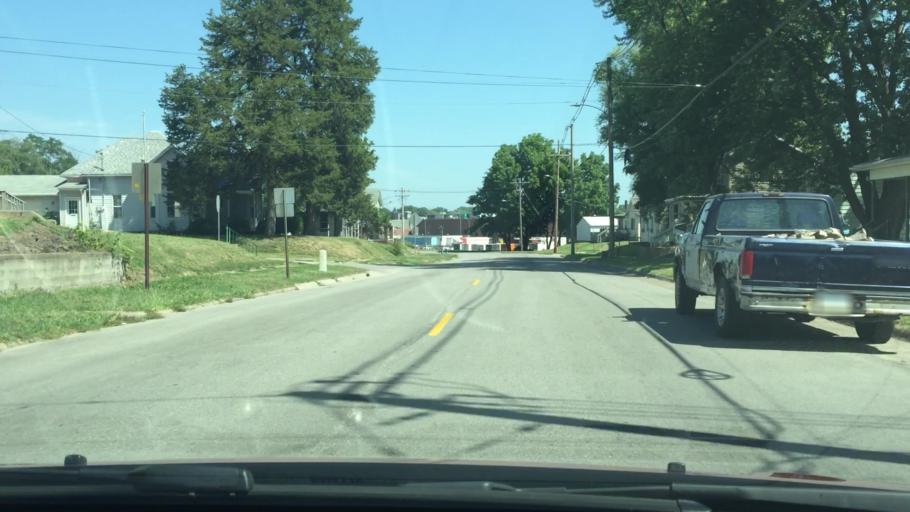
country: US
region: Iowa
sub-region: Muscatine County
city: Muscatine
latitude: 41.4342
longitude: -91.0430
